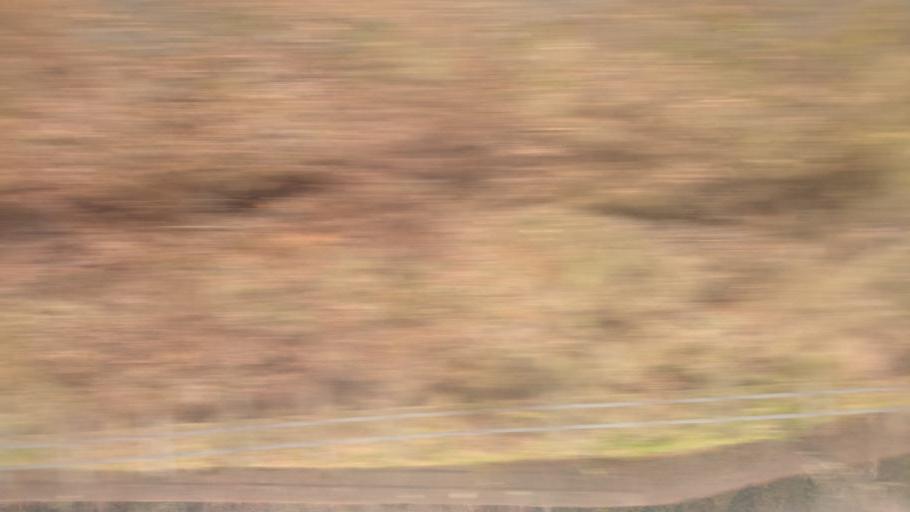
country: JP
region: Nagano
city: Shiojiri
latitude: 36.0518
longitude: 137.8965
